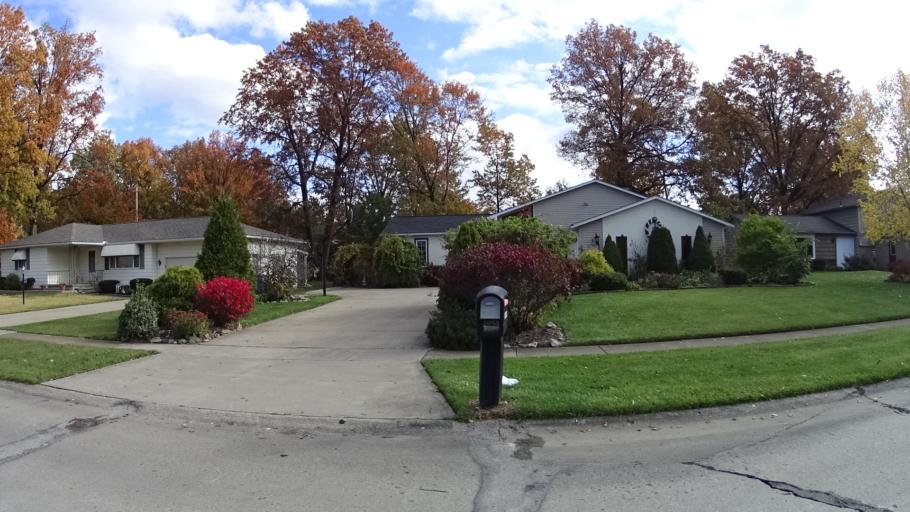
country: US
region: Ohio
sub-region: Lorain County
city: Lorain
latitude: 41.4229
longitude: -82.1981
